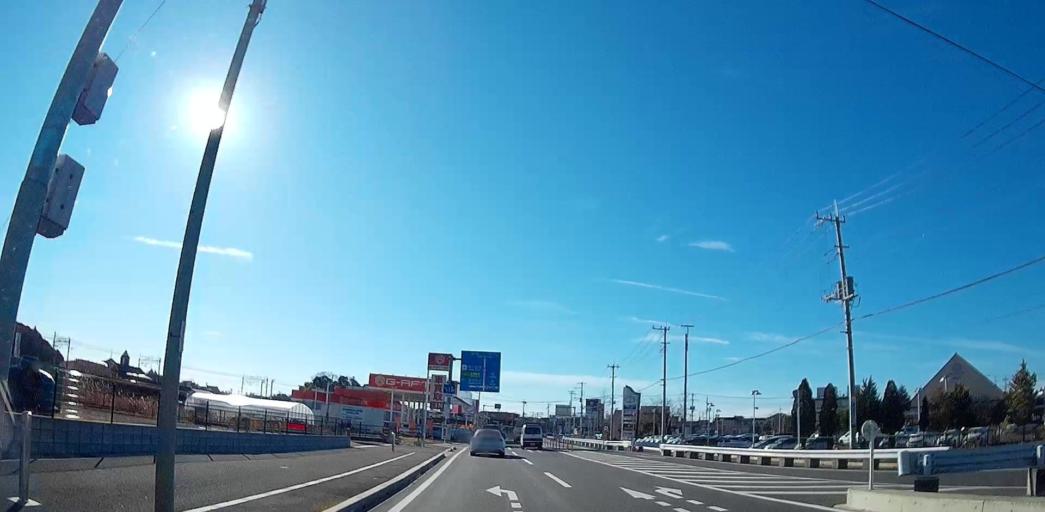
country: JP
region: Chiba
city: Narita
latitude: 35.7972
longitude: 140.3131
